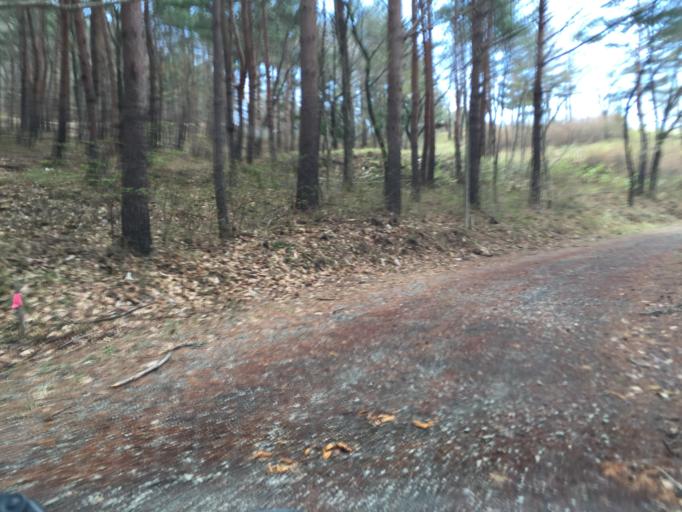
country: JP
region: Fukushima
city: Fukushima-shi
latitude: 37.8540
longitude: 140.4170
